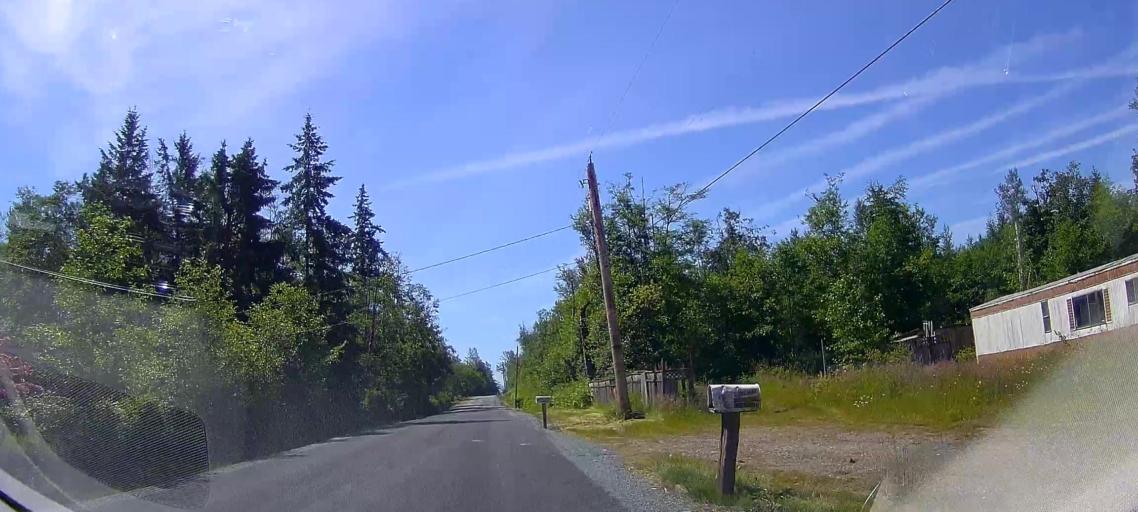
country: US
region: Washington
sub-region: Skagit County
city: Sedro-Woolley
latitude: 48.5377
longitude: -122.2483
